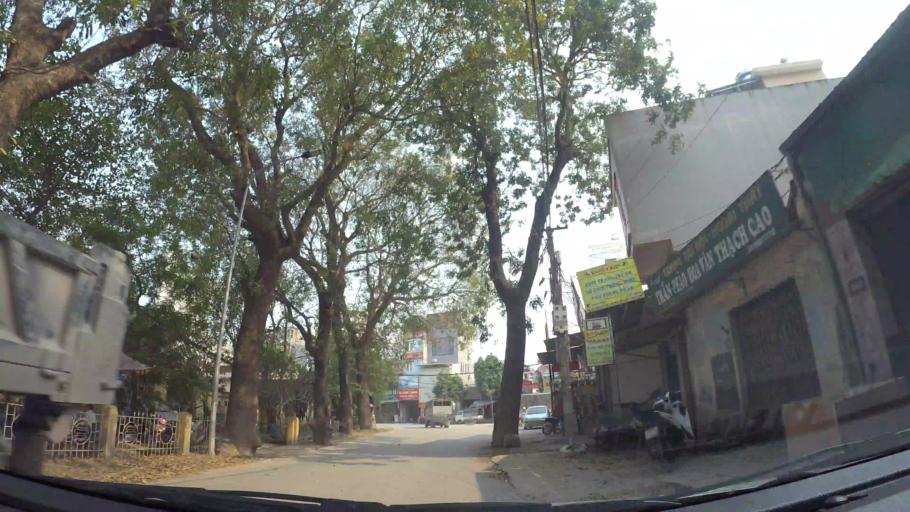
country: VN
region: Ha Noi
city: Ha Dong
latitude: 20.9961
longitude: 105.7526
